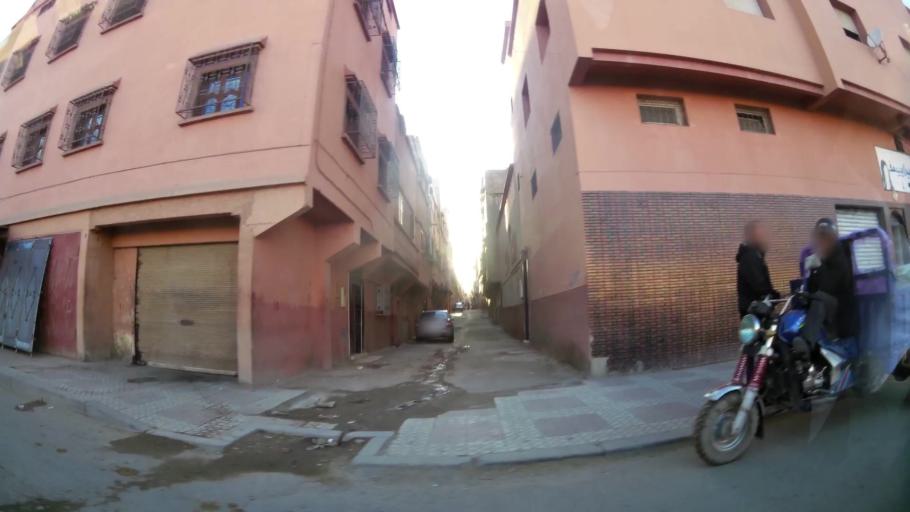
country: MA
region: Marrakech-Tensift-Al Haouz
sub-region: Kelaa-Des-Sraghna
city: Sidi Abdallah
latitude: 32.2405
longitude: -7.9497
